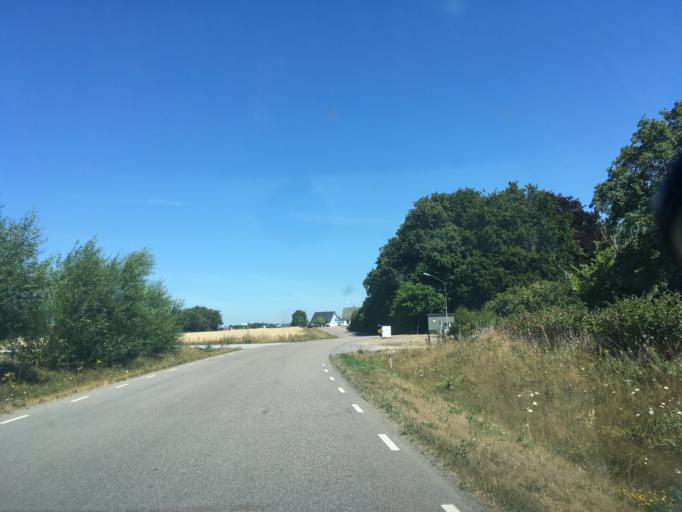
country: SE
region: Skane
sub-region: Trelleborgs Kommun
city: Skare
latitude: 55.3871
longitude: 13.0818
